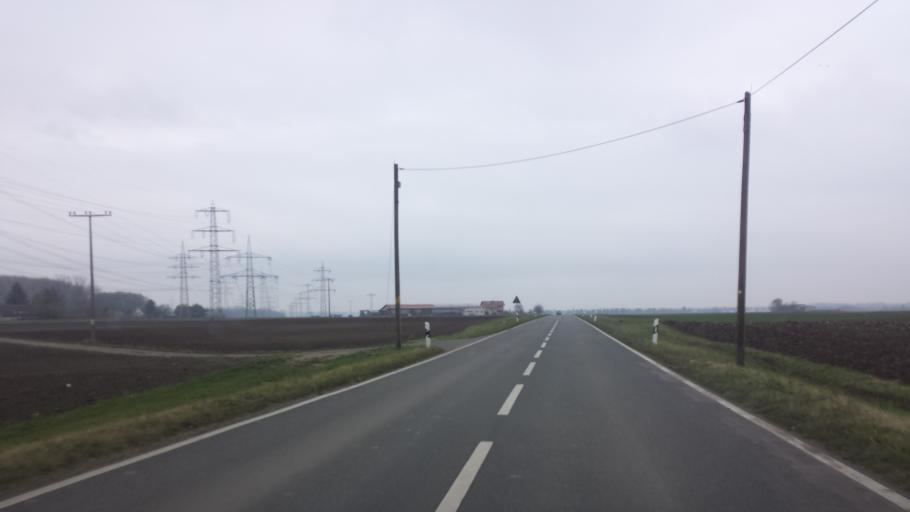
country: DE
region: Rheinland-Pfalz
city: Worms
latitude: 49.6614
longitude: 8.3938
